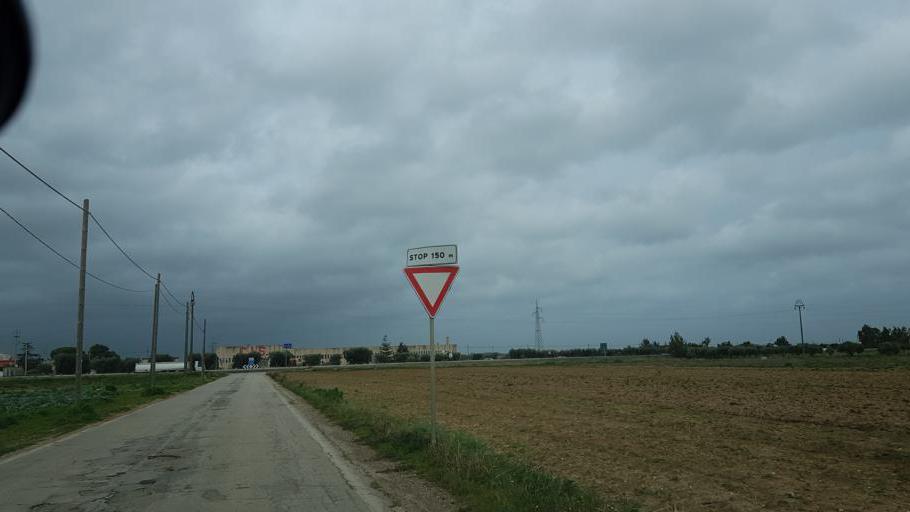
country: IT
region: Apulia
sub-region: Provincia di Brindisi
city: Brindisi
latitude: 40.6065
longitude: 17.8901
